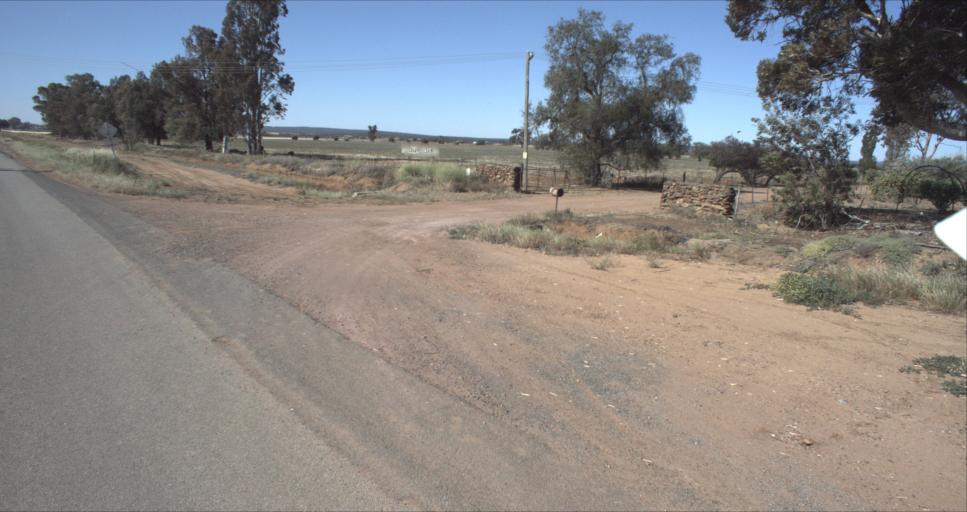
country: AU
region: New South Wales
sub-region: Leeton
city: Leeton
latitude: -34.4778
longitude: 146.3680
